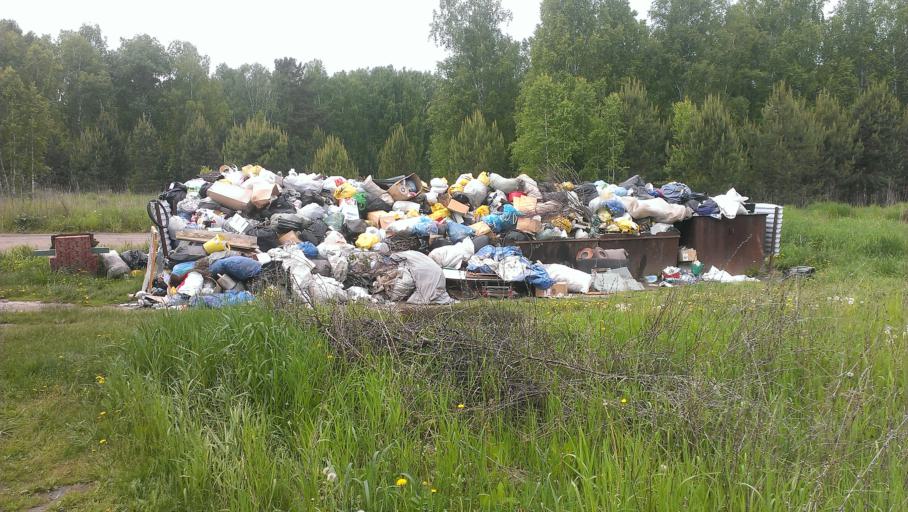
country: RU
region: Altai Krai
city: Bayunovskiye Klyuchi
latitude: 53.3321
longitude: 84.0980
